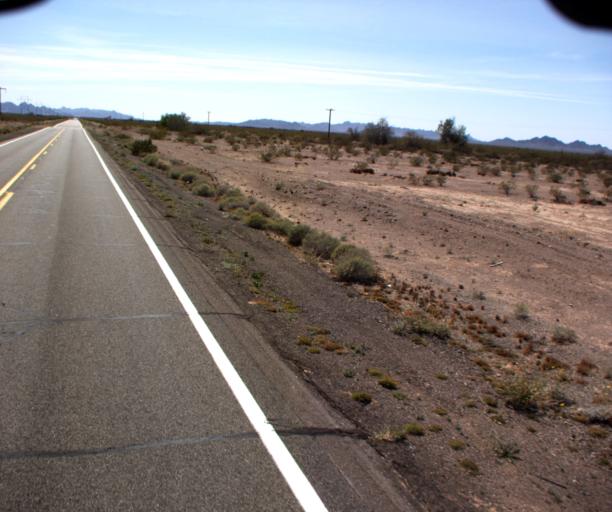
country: US
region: Arizona
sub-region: La Paz County
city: Quartzsite
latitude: 33.4390
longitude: -114.2171
